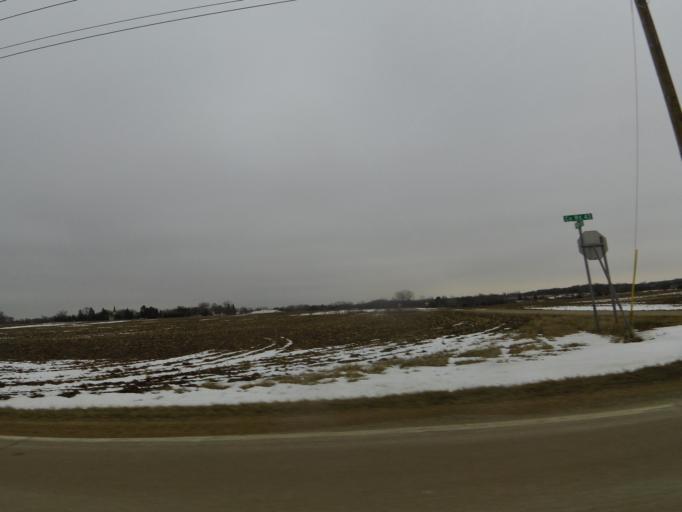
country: US
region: Minnesota
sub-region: Carver County
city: Carver
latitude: 44.7255
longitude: -93.6844
